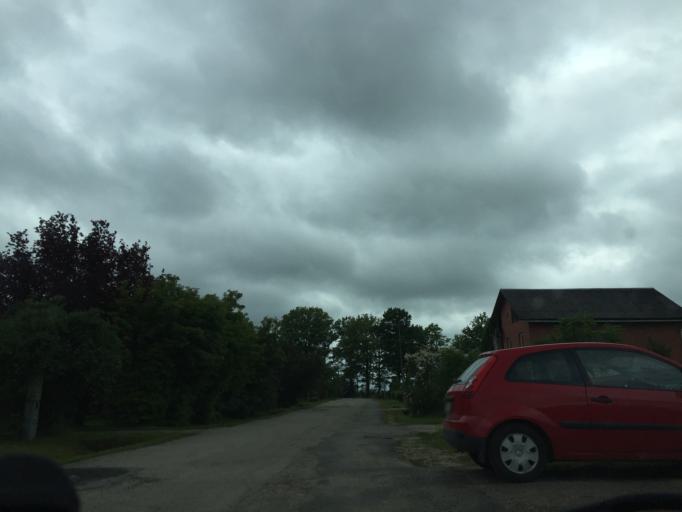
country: LV
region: Valmieras Rajons
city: Valmiera
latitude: 57.5539
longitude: 25.4191
